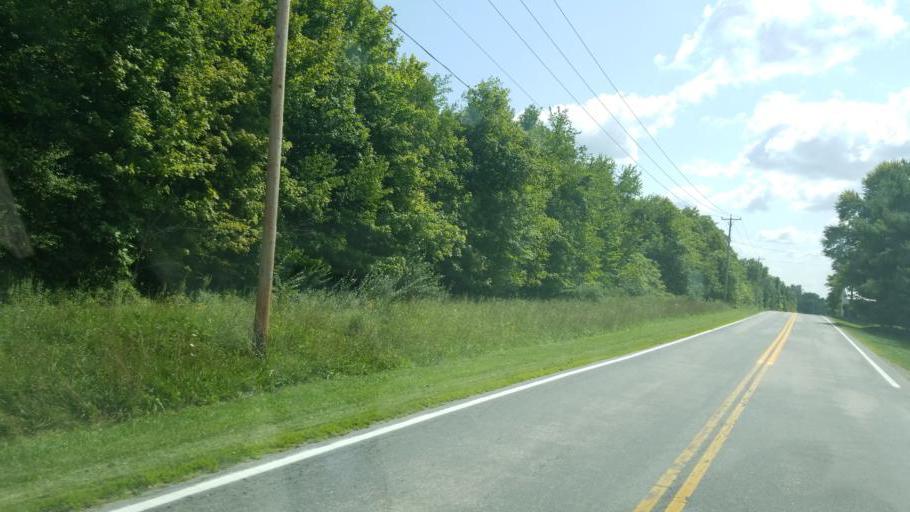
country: US
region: Ohio
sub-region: Delaware County
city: Lewis Center
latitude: 40.2461
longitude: -82.9593
